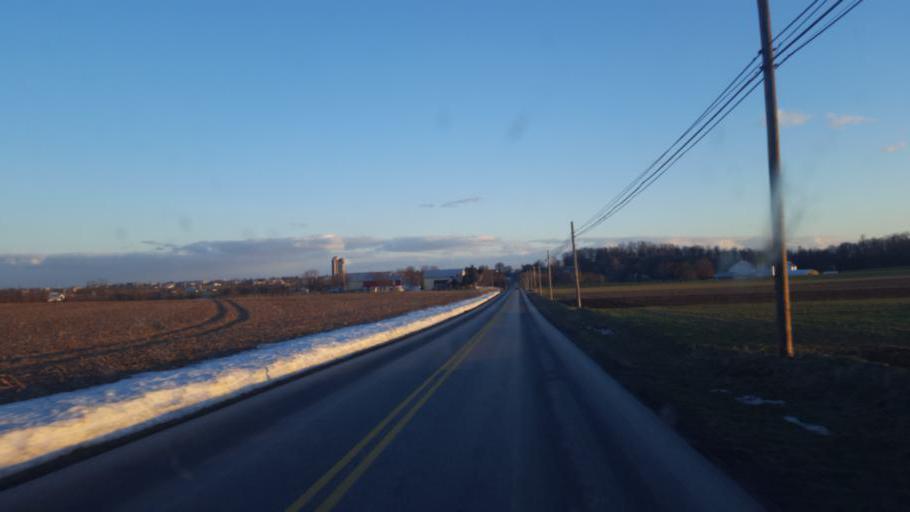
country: US
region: Pennsylvania
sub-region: Lancaster County
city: Intercourse
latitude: 40.0655
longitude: -76.1046
